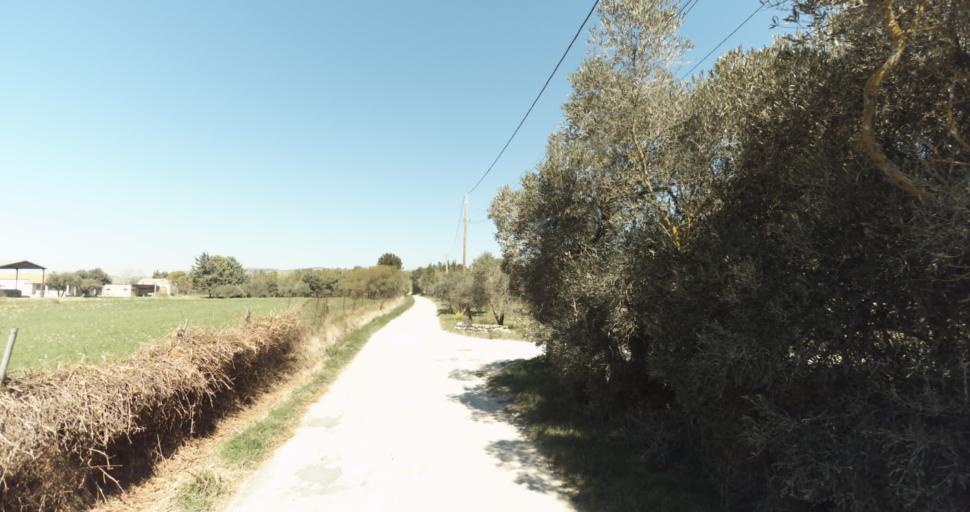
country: FR
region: Provence-Alpes-Cote d'Azur
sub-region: Departement des Bouches-du-Rhone
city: Pelissanne
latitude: 43.6158
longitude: 5.1574
